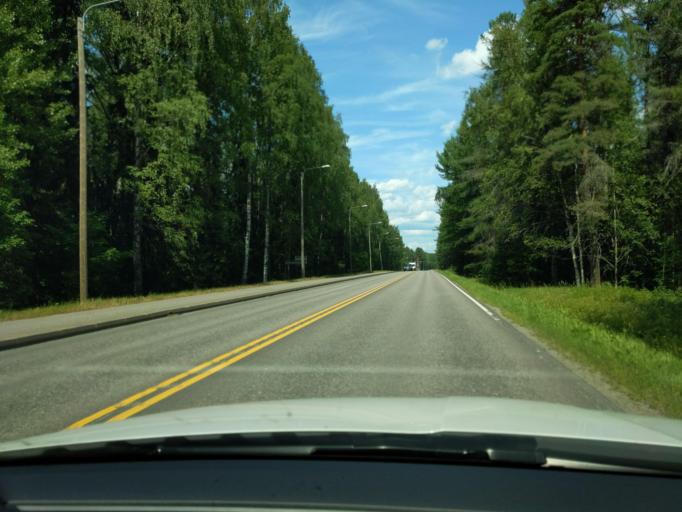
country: FI
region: Paijanne Tavastia
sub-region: Lahti
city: Heinola
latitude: 61.1723
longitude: 25.9914
